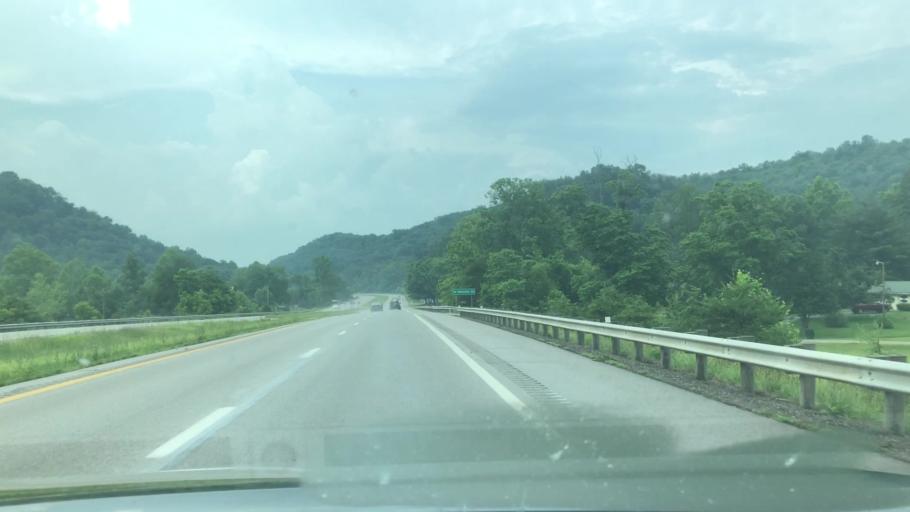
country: US
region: Ohio
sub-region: Jackson County
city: Jackson
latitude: 39.1448
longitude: -82.7263
